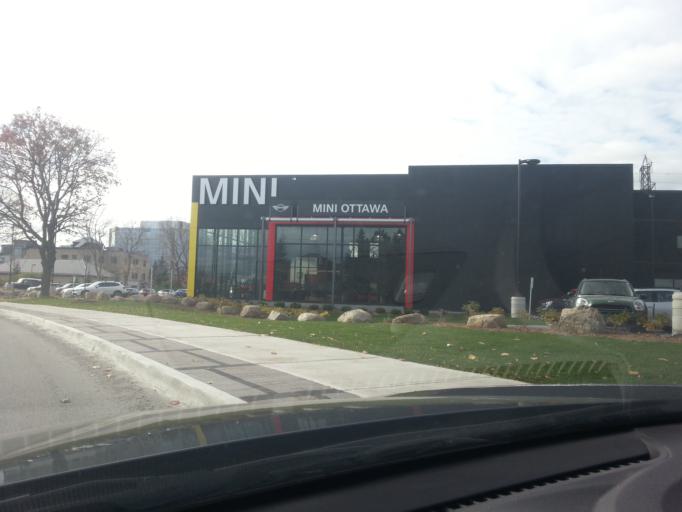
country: CA
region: Ontario
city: Ottawa
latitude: 45.3840
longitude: -75.7418
